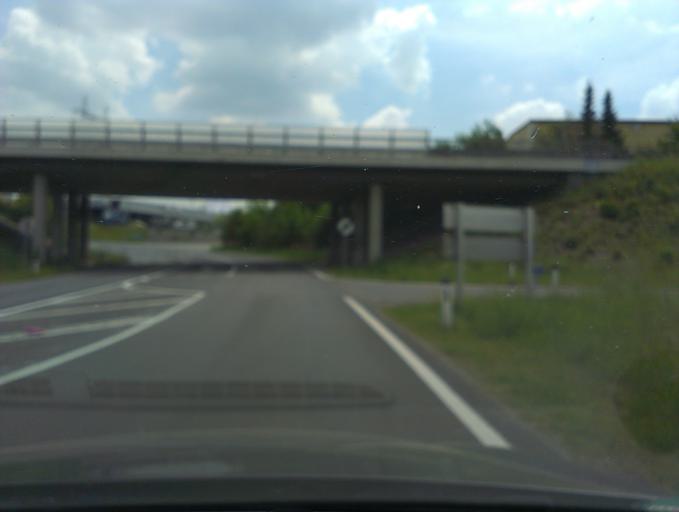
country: AT
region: Upper Austria
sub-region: Politischer Bezirk Braunau am Inn
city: Braunau am Inn
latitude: 48.2472
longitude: 13.0525
